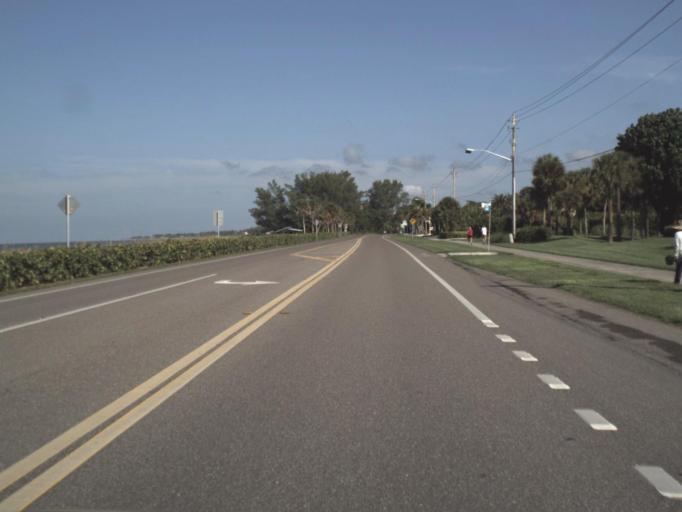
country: US
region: Florida
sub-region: Manatee County
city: Longboat Key
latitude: 27.3842
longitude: -82.6388
